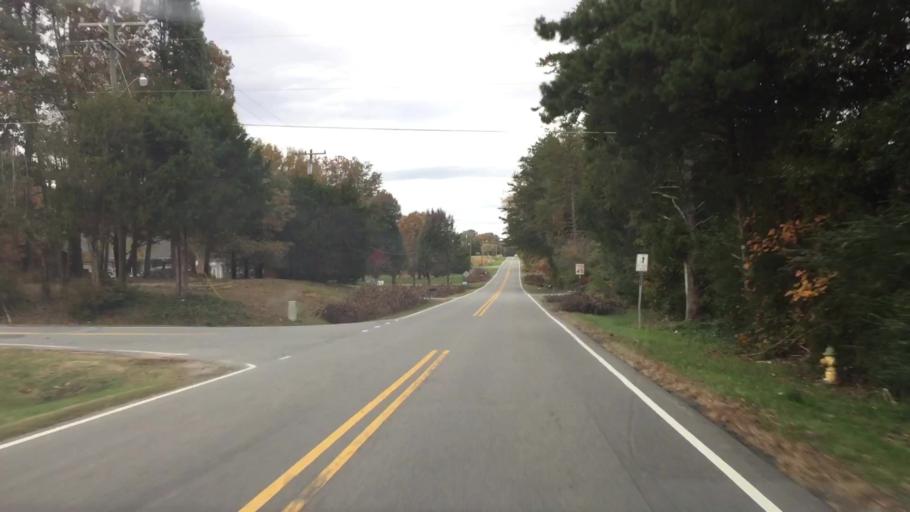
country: US
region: North Carolina
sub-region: Rockingham County
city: Reidsville
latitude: 36.3408
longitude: -79.6997
